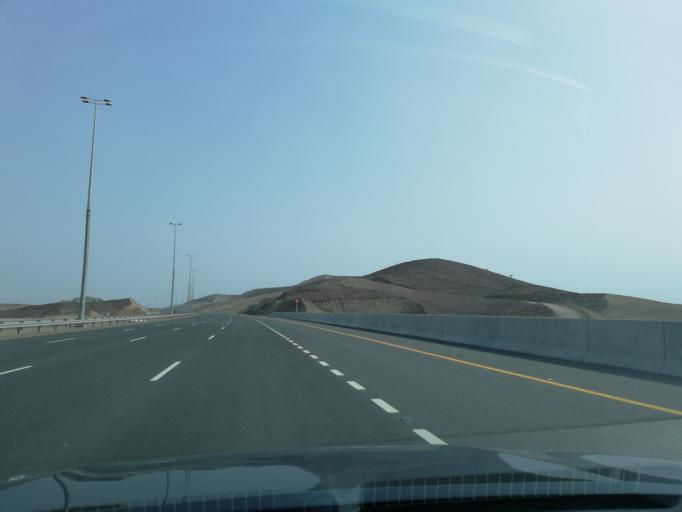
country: OM
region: Al Batinah
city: Al Liwa'
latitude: 24.3558
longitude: 56.5498
